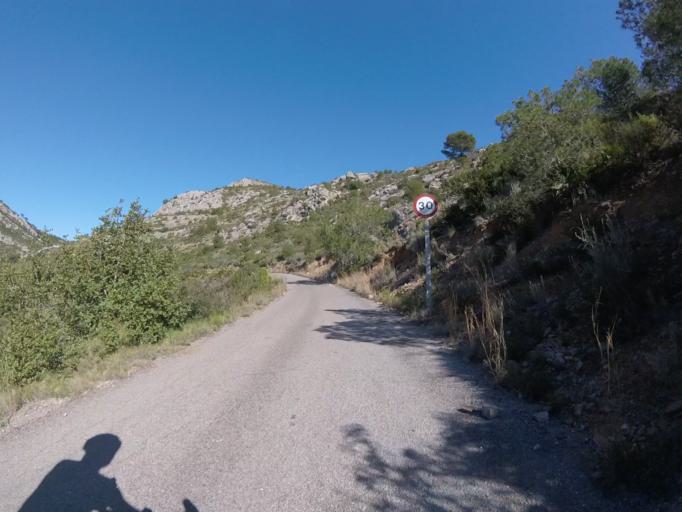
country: ES
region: Valencia
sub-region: Provincia de Castello
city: Orpesa/Oropesa del Mar
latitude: 40.0764
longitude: 0.1081
